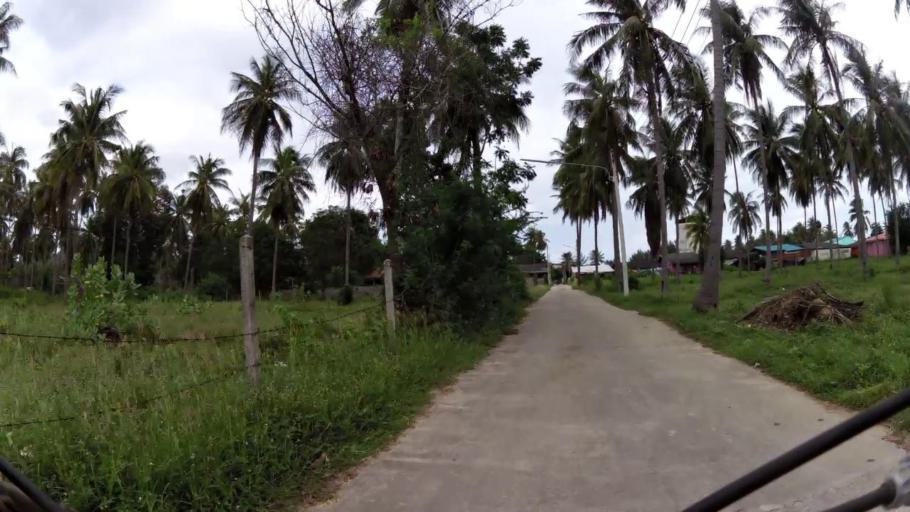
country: TH
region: Prachuap Khiri Khan
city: Prachuap Khiri Khan
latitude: 11.7386
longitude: 99.7779
